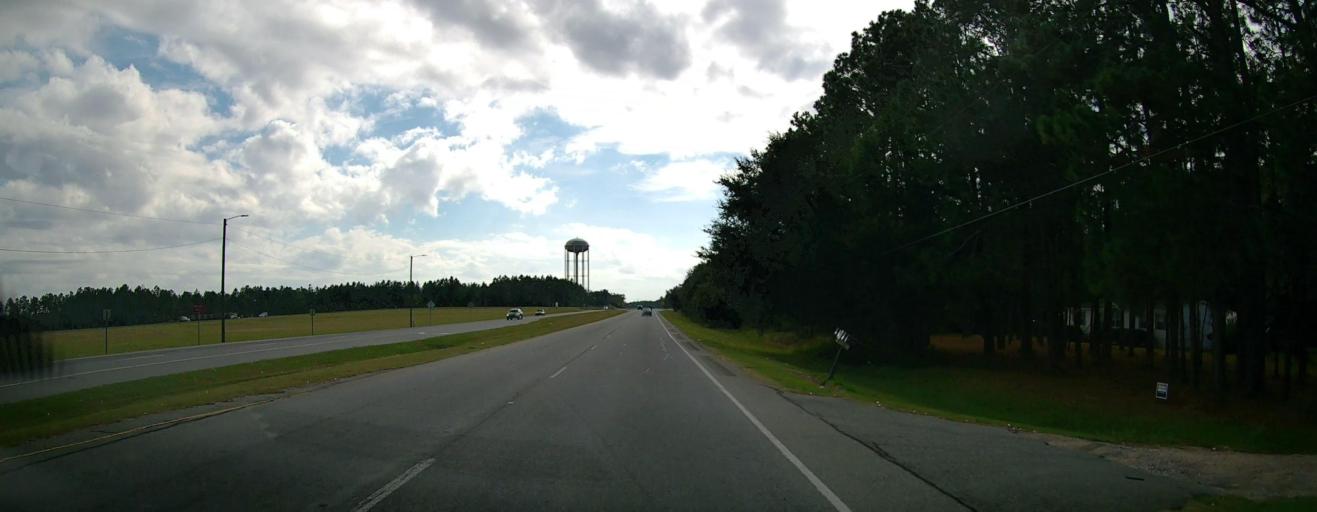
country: US
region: Georgia
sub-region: Mitchell County
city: Camilla
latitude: 31.2813
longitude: -84.1881
